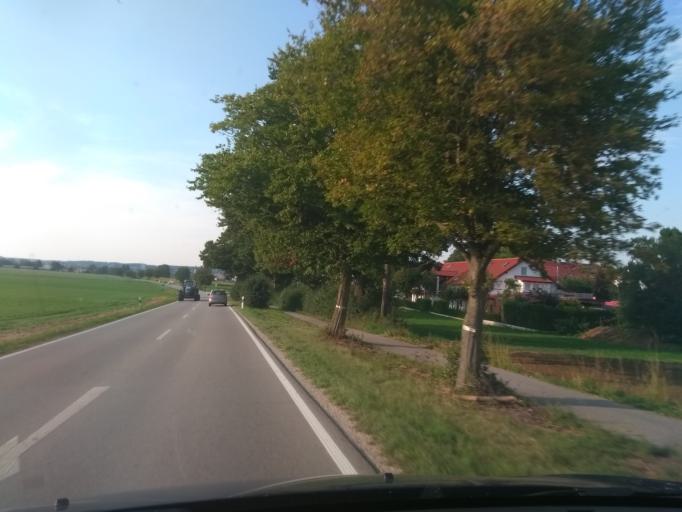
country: DE
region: Bavaria
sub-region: Upper Bavaria
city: Markt Indersdorf
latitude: 48.3405
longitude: 11.3883
